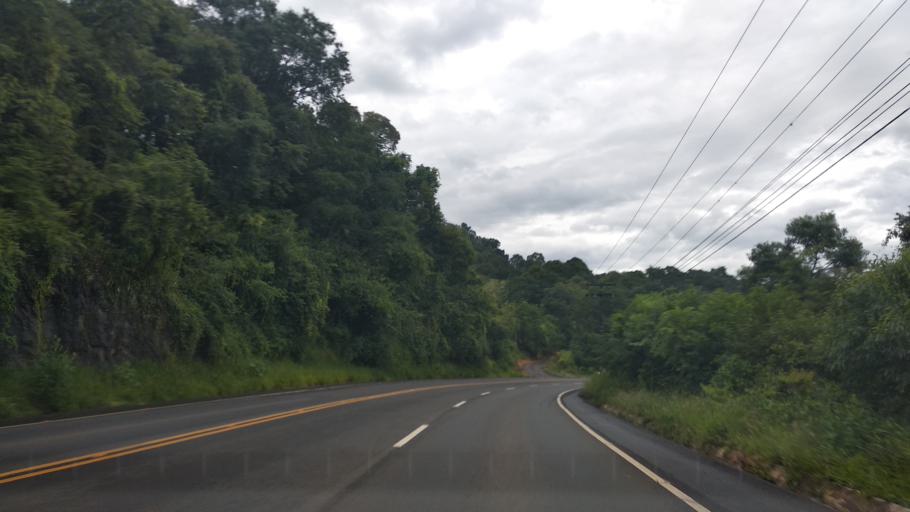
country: BR
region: Santa Catarina
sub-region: Videira
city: Videira
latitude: -27.0637
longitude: -51.2275
